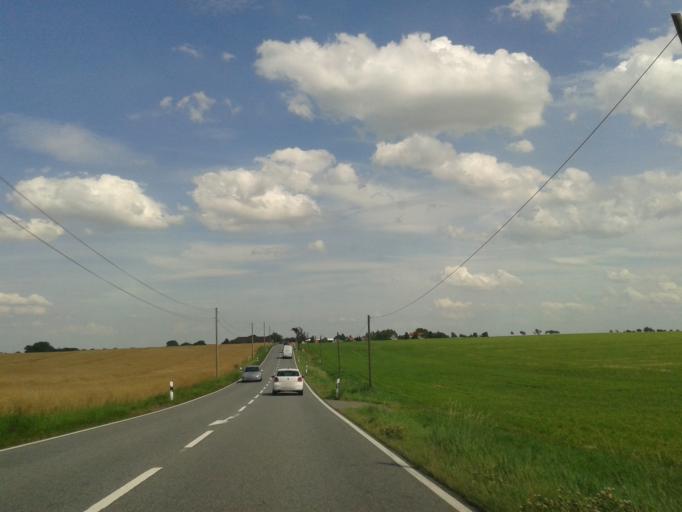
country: DE
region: Saxony
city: Reinsberg
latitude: 51.0523
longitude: 13.4005
